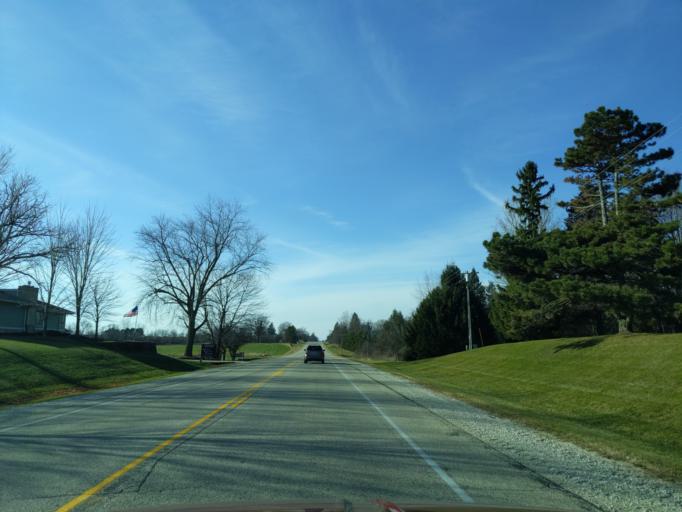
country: US
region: Wisconsin
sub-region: Walworth County
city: Whitewater
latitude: 42.8277
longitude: -88.7970
